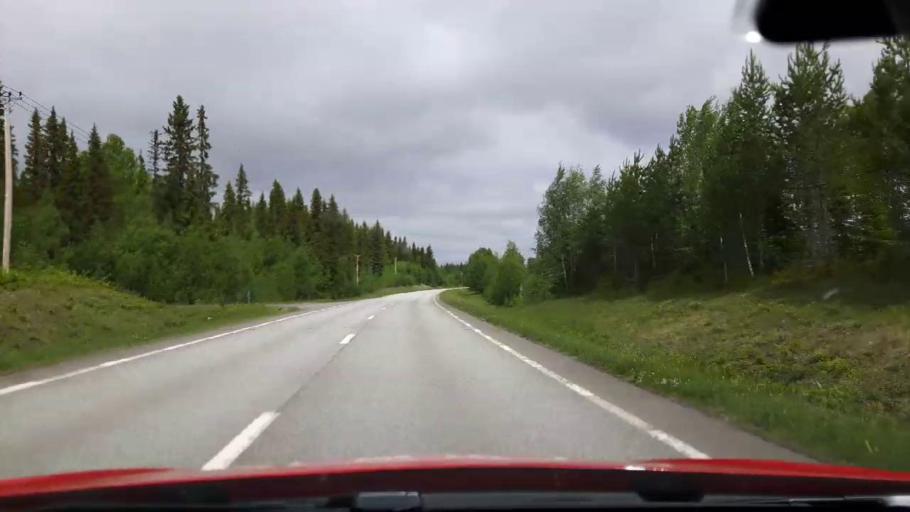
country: SE
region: Jaemtland
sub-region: Krokoms Kommun
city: Krokom
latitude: 63.4933
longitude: 14.5075
